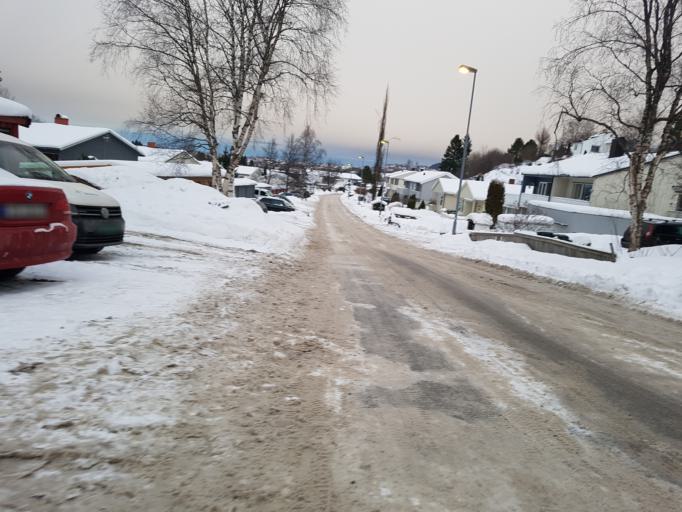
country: NO
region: Sor-Trondelag
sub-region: Trondheim
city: Trondheim
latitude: 63.3713
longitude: 10.3866
